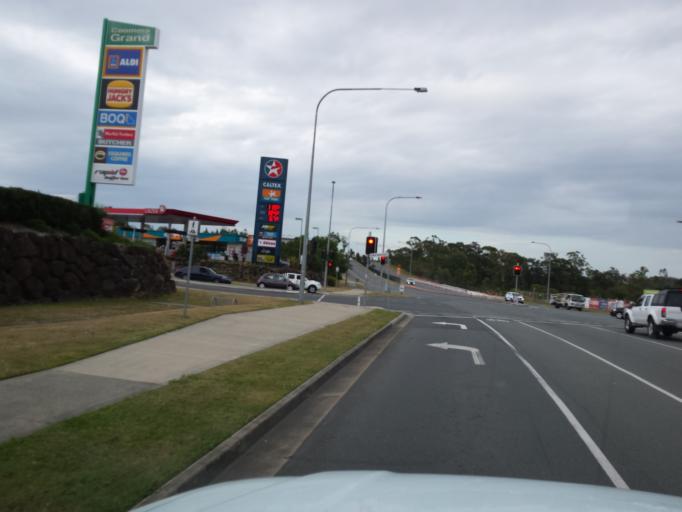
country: AU
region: Queensland
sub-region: Gold Coast
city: Oxenford
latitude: -27.8503
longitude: 153.3001
